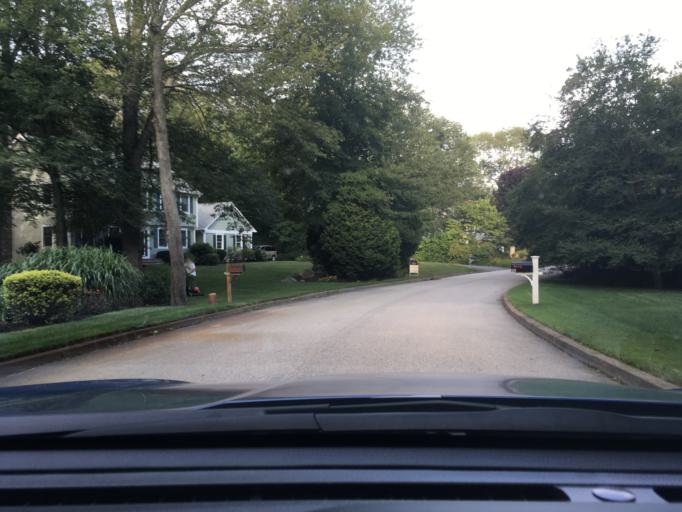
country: US
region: Rhode Island
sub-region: Washington County
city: Exeter
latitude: 41.6159
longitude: -71.5093
